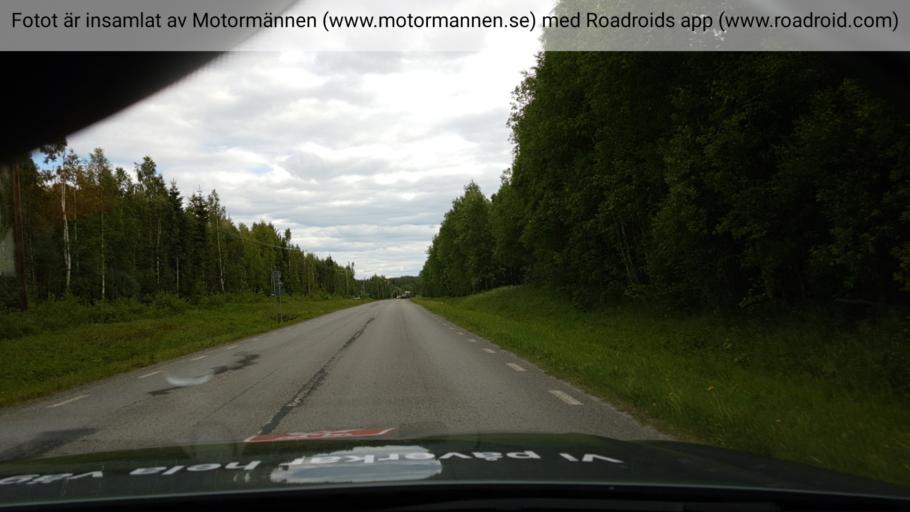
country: SE
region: Jaemtland
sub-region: Stroemsunds Kommun
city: Stroemsund
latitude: 63.8957
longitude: 15.5376
